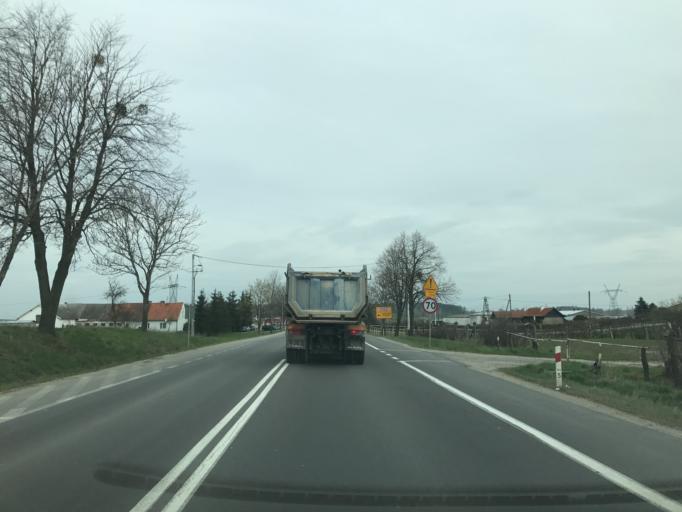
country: PL
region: Warmian-Masurian Voivodeship
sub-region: Powiat ostrodzki
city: Gierzwald
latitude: 53.5939
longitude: 20.0818
